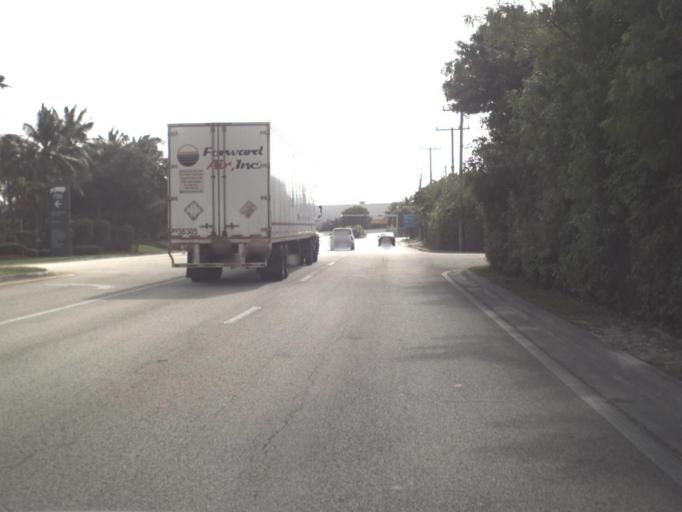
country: US
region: Florida
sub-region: Miami-Dade County
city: Virginia Gardens
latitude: 25.7958
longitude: -80.3067
